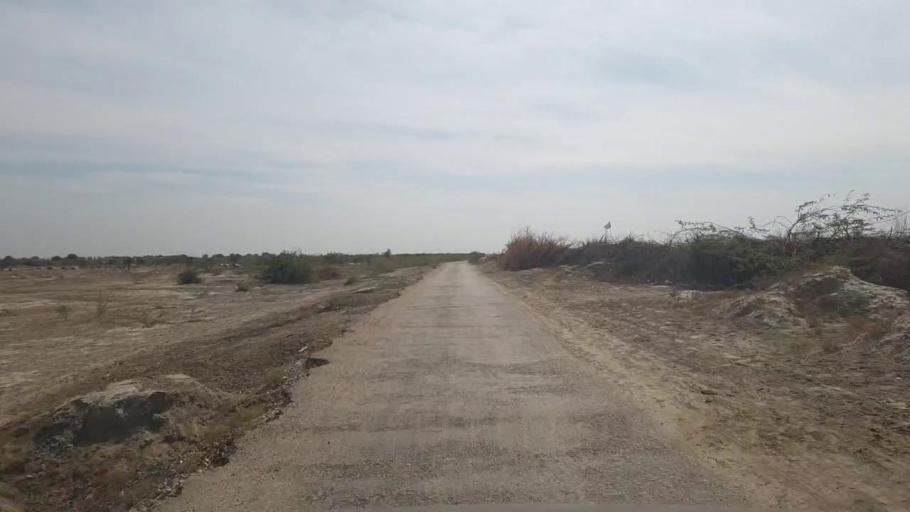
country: PK
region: Sindh
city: Kunri
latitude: 25.2639
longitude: 69.6034
